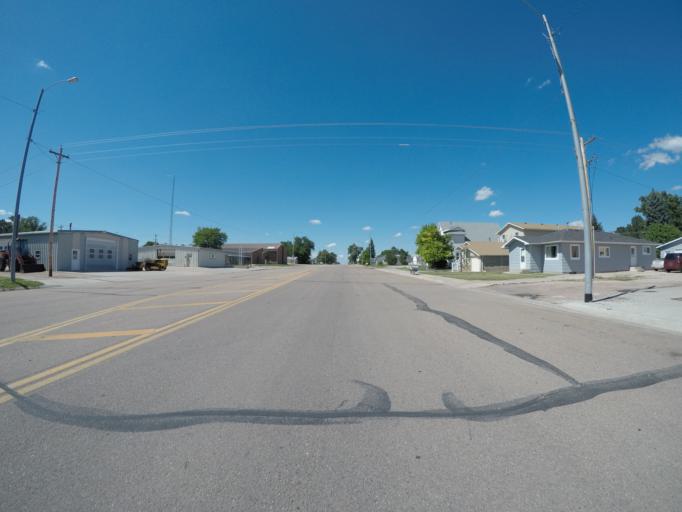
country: US
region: Nebraska
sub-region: Chase County
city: Imperial
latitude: 40.5237
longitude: -101.6431
